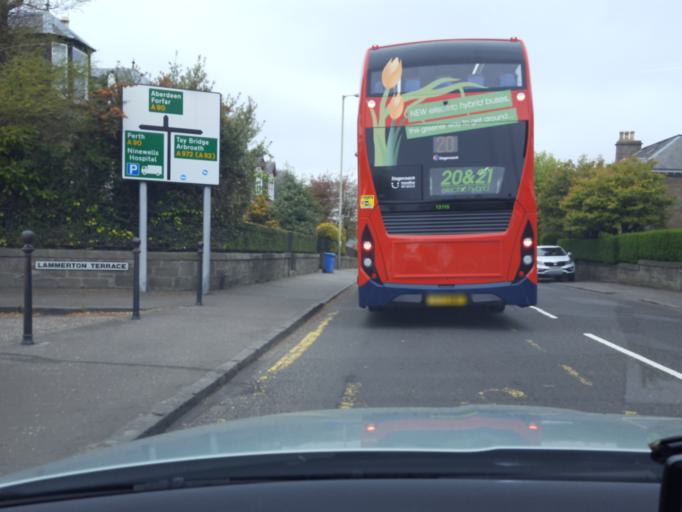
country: GB
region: Scotland
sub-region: Dundee City
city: Dundee
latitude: 56.4784
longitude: -2.9529
